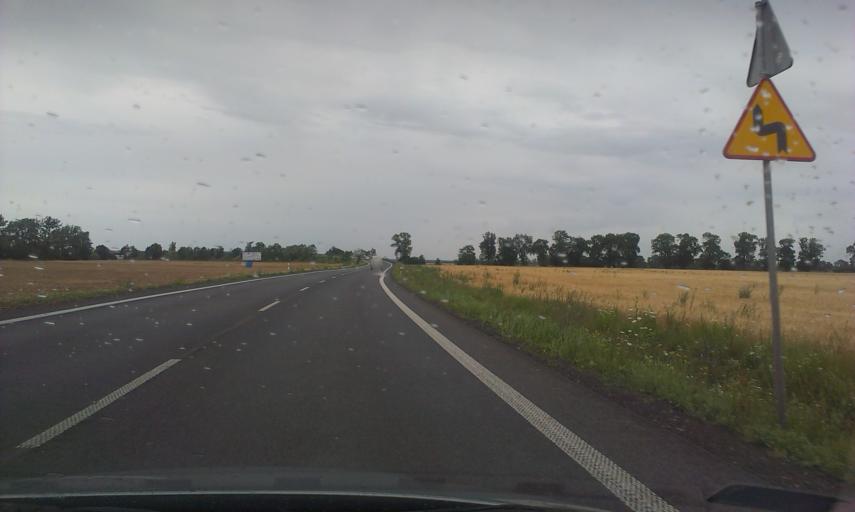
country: PL
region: Greater Poland Voivodeship
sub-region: Powiat obornicki
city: Oborniki
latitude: 52.5975
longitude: 16.8237
